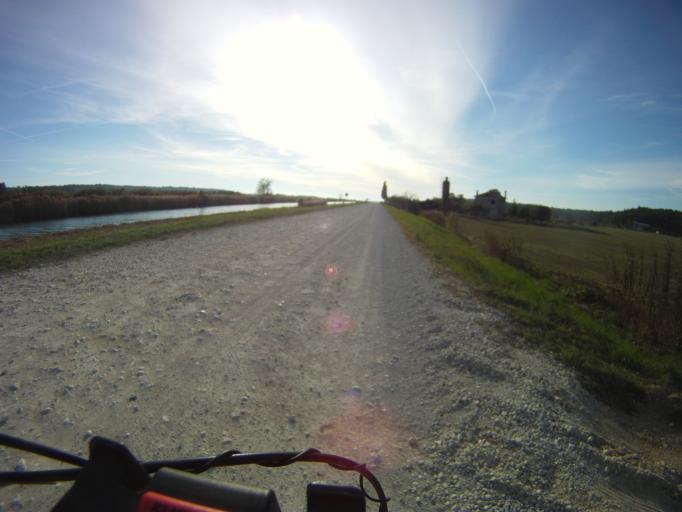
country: HR
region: Istarska
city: Novigrad
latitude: 45.3210
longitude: 13.6059
